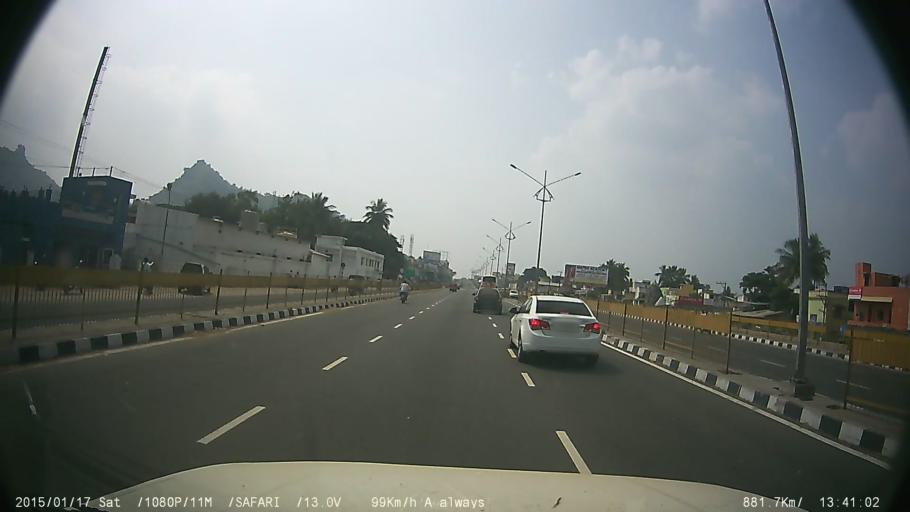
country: IN
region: Tamil Nadu
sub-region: Vellore
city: Vellore
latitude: 12.9365
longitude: 79.1592
